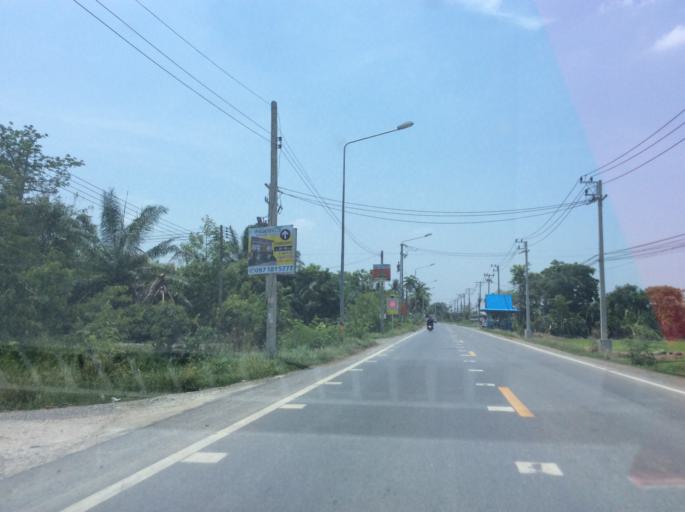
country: TH
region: Pathum Thani
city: Ban Rangsit
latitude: 14.0155
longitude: 100.7795
